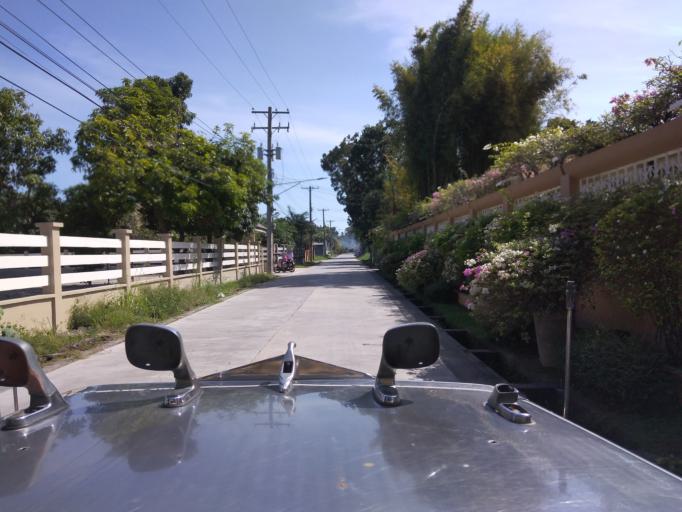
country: PH
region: Central Luzon
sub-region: Province of Pampanga
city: Bacolor
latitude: 15.0058
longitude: 120.6616
